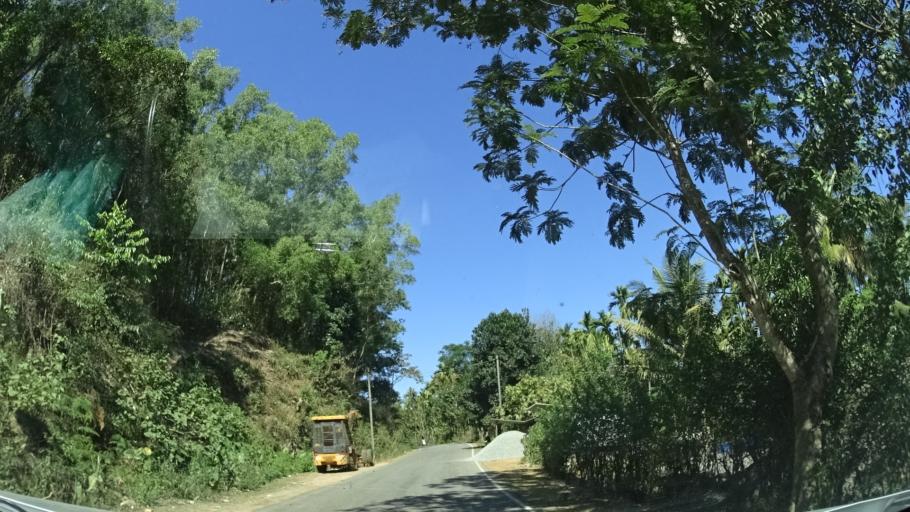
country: IN
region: Karnataka
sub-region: Chikmagalur
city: Sringeri
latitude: 13.2280
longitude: 75.3572
